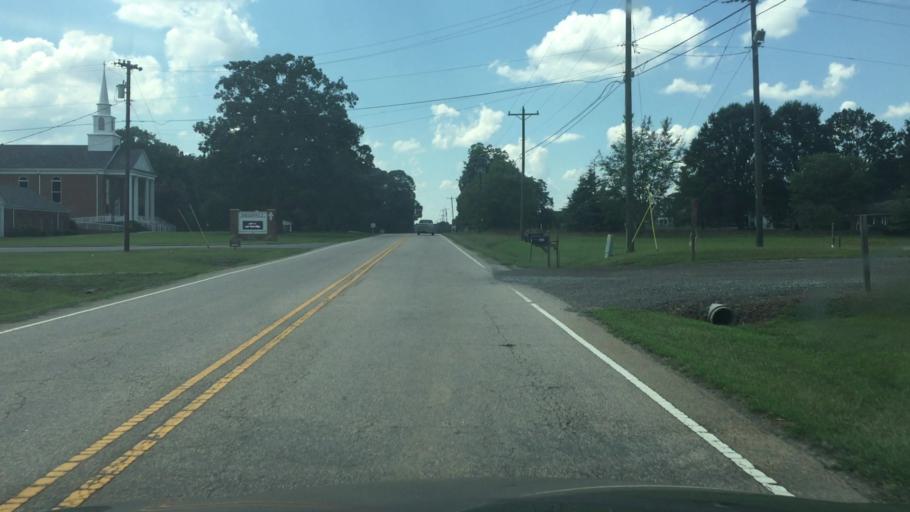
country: US
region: North Carolina
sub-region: Iredell County
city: Mooresville
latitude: 35.5849
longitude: -80.7423
